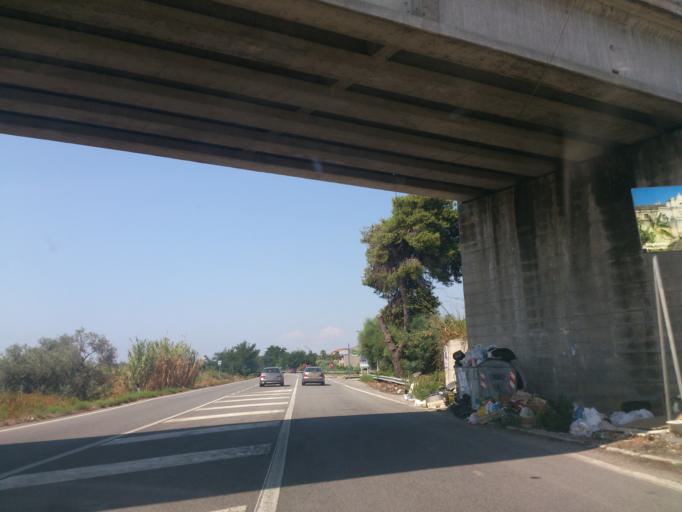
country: IT
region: Calabria
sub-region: Provincia di Reggio Calabria
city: Caulonia Marina
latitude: 38.3599
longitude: 16.4905
